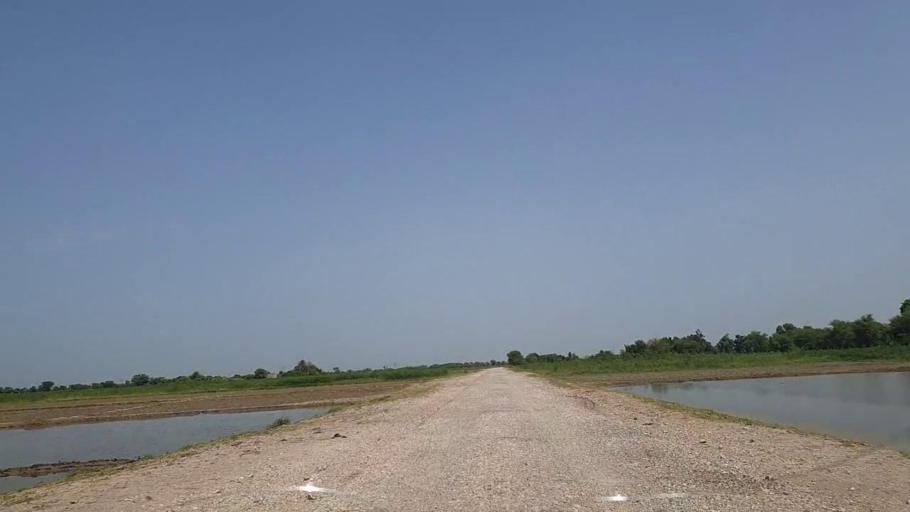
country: PK
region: Sindh
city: Kandiaro
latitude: 27.0147
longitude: 68.1681
